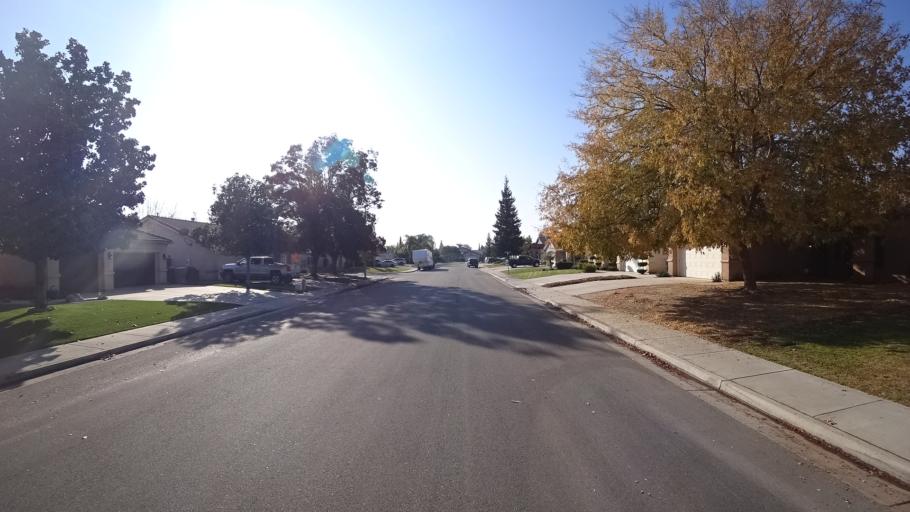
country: US
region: California
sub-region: Kern County
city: Greenacres
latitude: 35.3656
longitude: -119.1128
